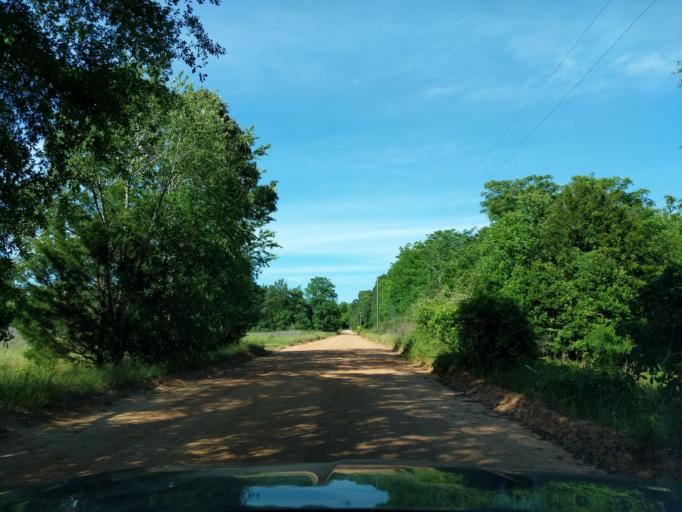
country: US
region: Georgia
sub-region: Jefferson County
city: Wrens
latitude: 33.2233
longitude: -82.3528
